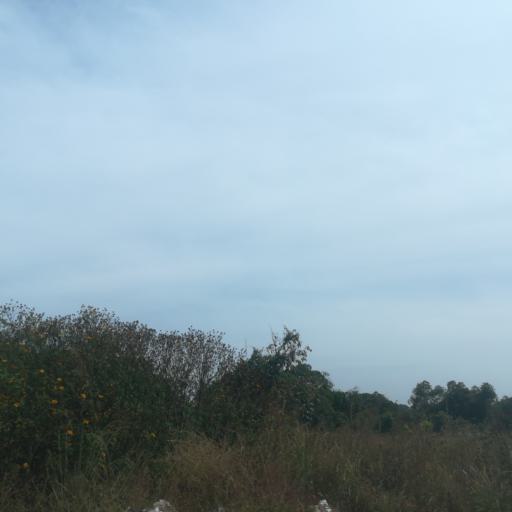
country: NG
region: Plateau
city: Jos
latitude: 9.8876
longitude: 8.8413
